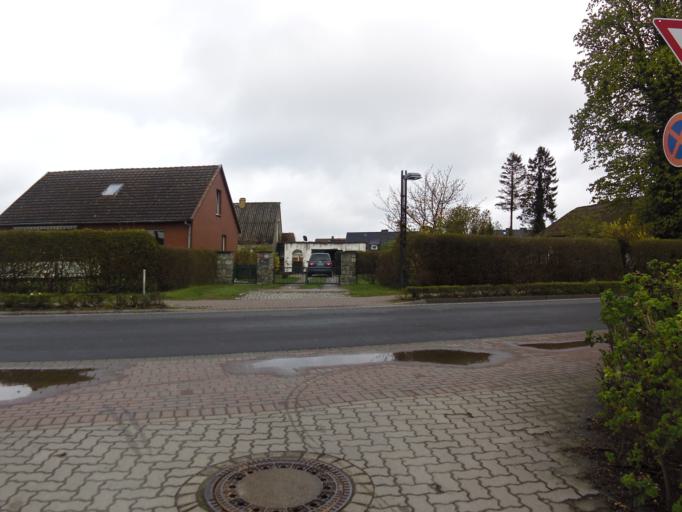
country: DE
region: Mecklenburg-Vorpommern
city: Zingst
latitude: 54.4339
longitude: 12.6912
